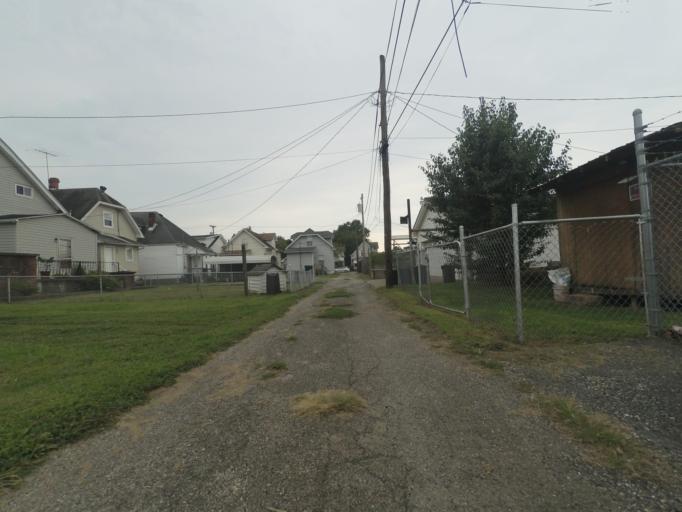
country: US
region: West Virginia
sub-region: Cabell County
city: Huntington
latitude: 38.4162
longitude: -82.4328
